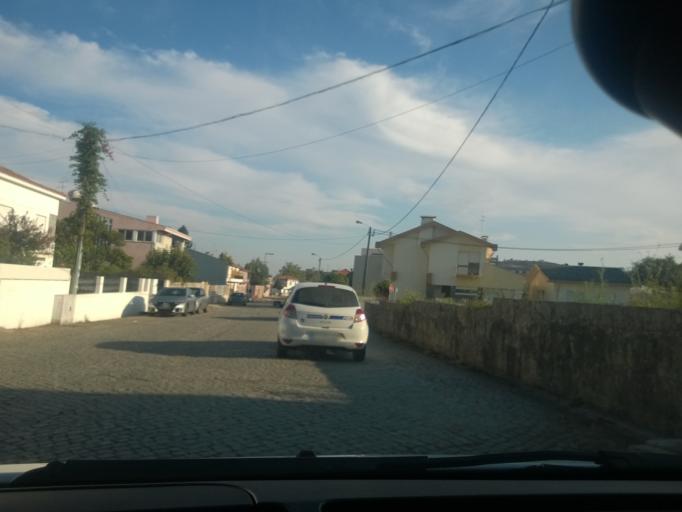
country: PT
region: Porto
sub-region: Maia
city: Anta
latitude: 41.2646
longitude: -8.6184
